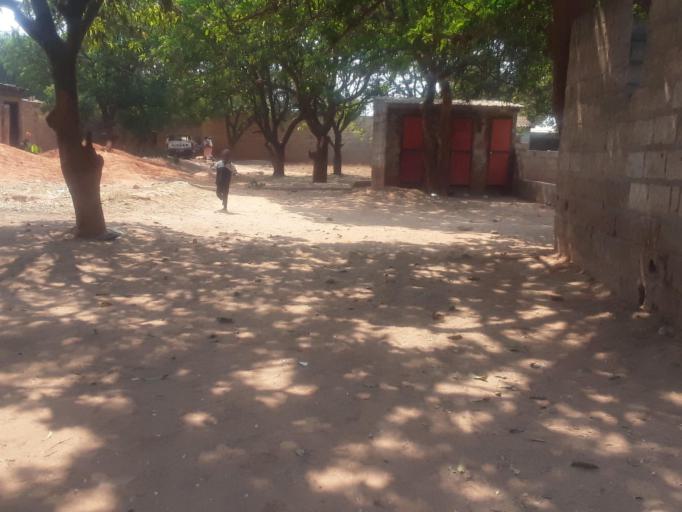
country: ZM
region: Lusaka
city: Lusaka
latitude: -15.3530
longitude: 28.2936
